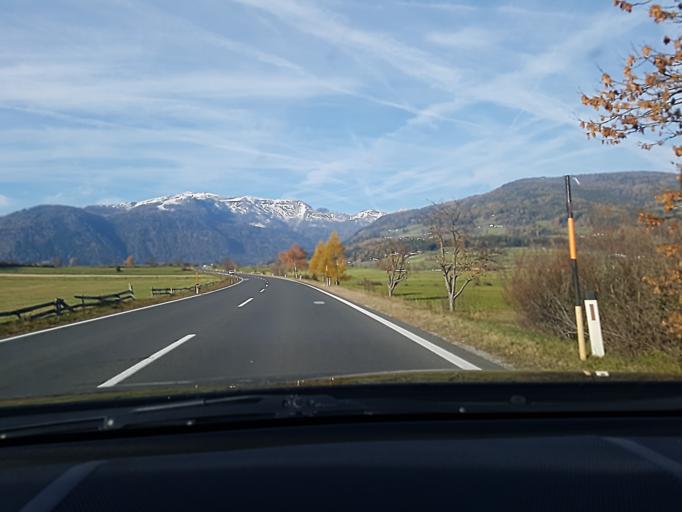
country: AT
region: Salzburg
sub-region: Politischer Bezirk Tamsweg
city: Mariapfarr
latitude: 47.1421
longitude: 13.7281
